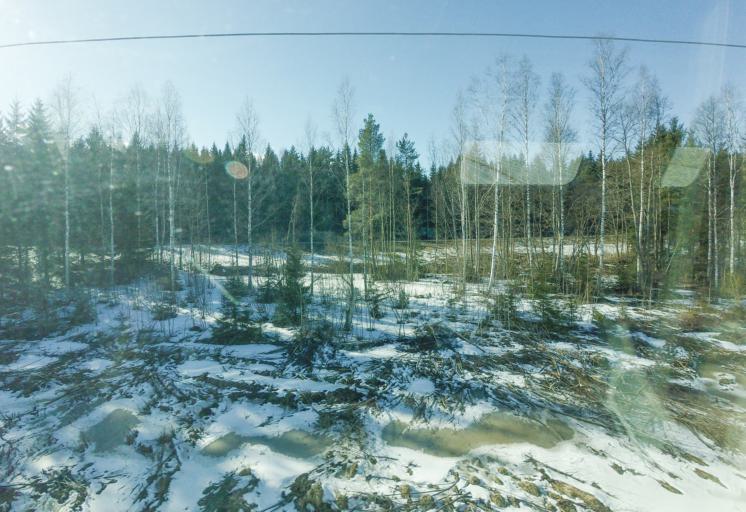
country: FI
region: South Karelia
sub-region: Imatra
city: Parikkala
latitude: 61.5120
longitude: 29.5087
